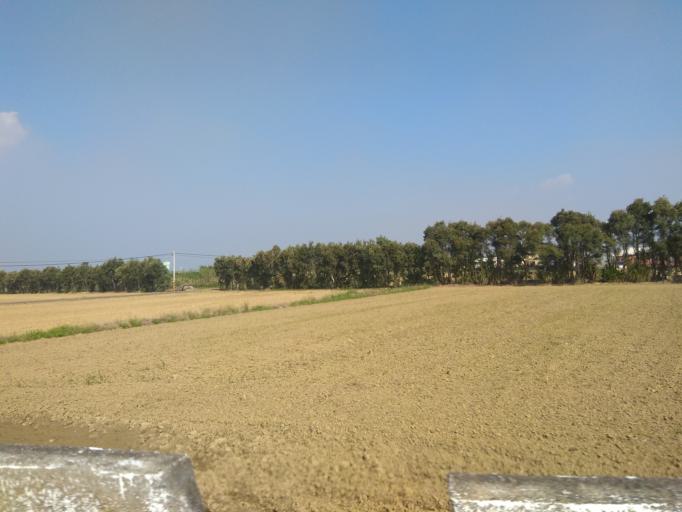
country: TW
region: Taiwan
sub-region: Hsinchu
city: Zhubei
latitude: 24.9906
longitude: 121.0718
